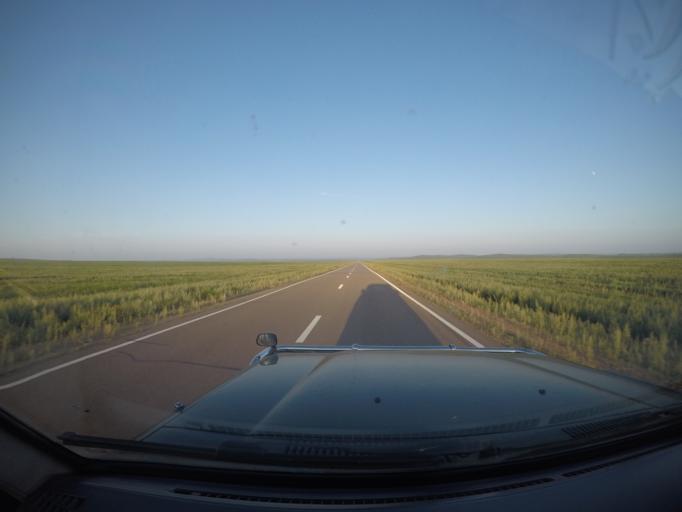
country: MN
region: Suhbaatar
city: Hanhohiy
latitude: 47.5705
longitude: 112.2474
